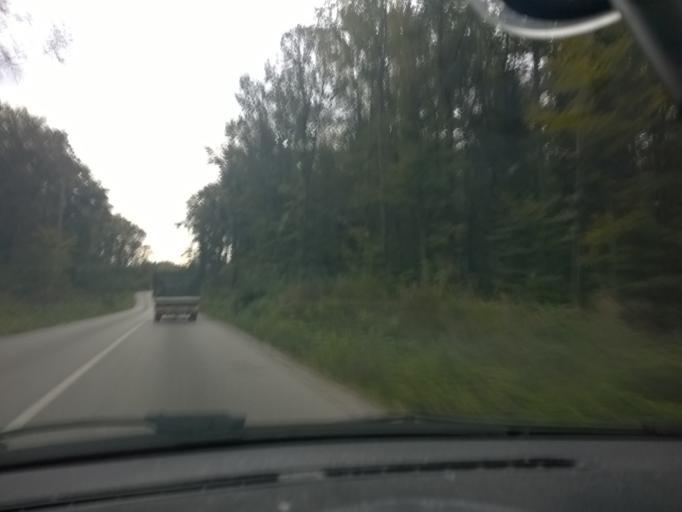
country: HR
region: Zagrebacka
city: Pojatno
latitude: 45.8937
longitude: 15.7951
